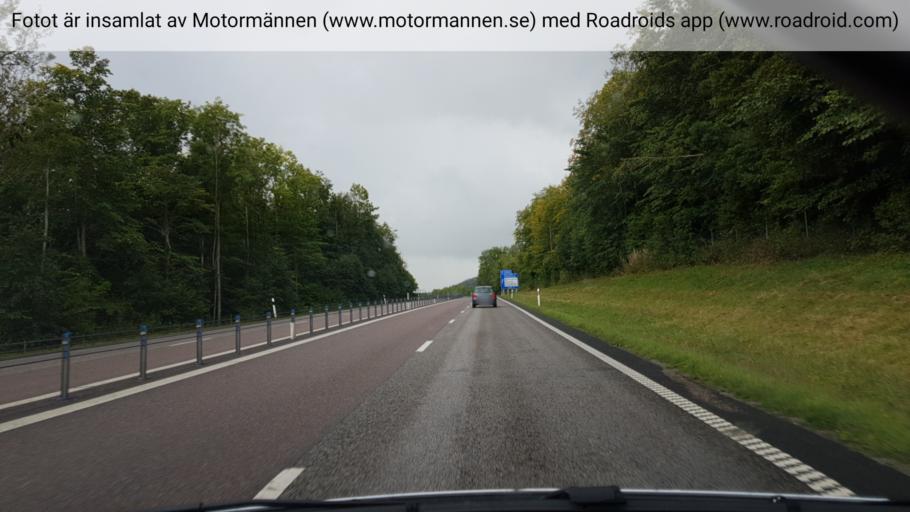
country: SE
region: Vaestra Goetaland
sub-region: Skovde Kommun
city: Skultorp
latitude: 58.3169
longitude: 13.8146
